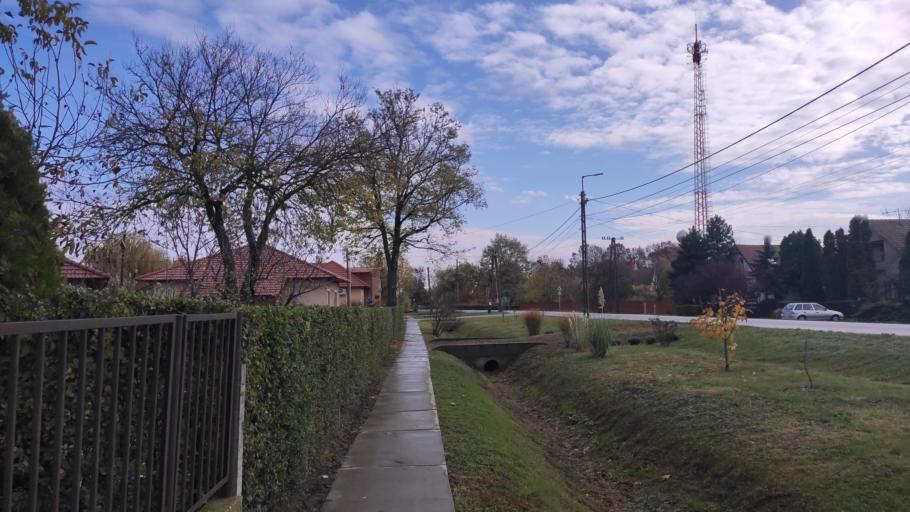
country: HU
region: Bekes
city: Mezobereny
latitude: 46.7618
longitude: 21.0397
